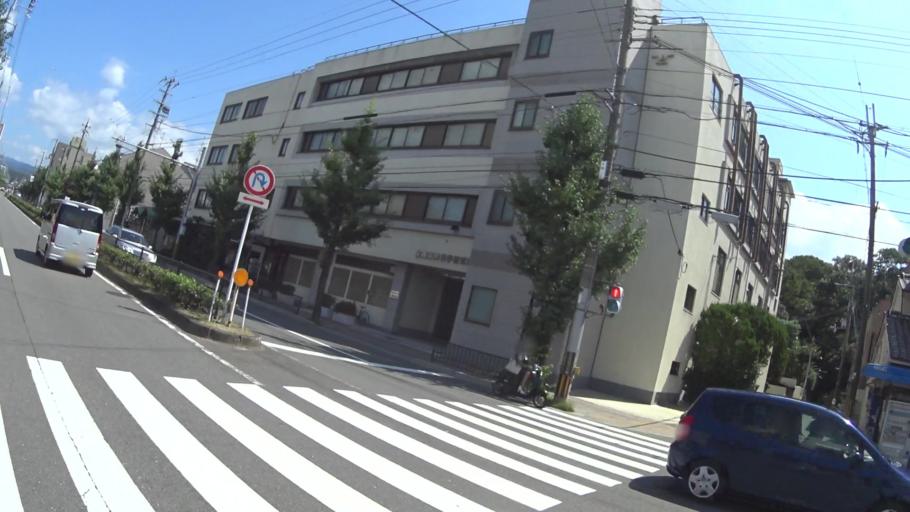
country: JP
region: Kyoto
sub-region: Kyoto-shi
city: Kamigyo-ku
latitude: 35.0370
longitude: 135.7709
